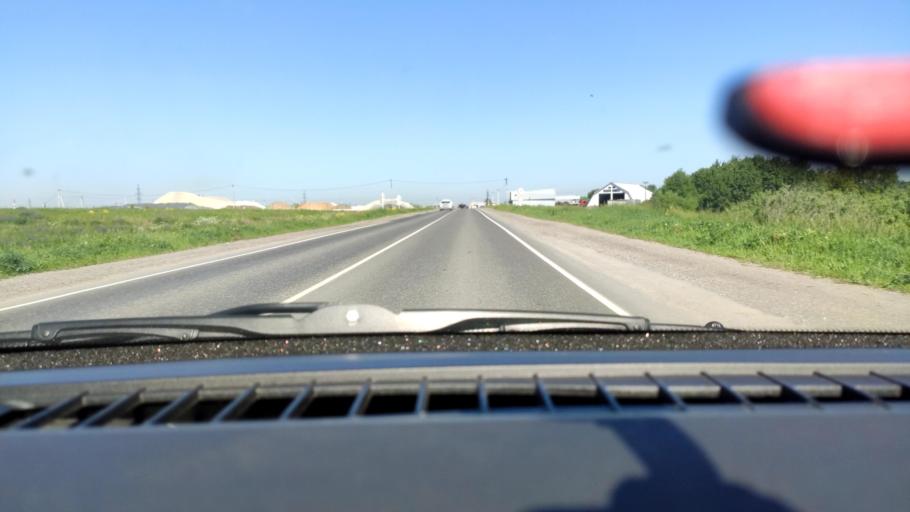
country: RU
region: Perm
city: Froly
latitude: 57.9059
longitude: 56.1988
